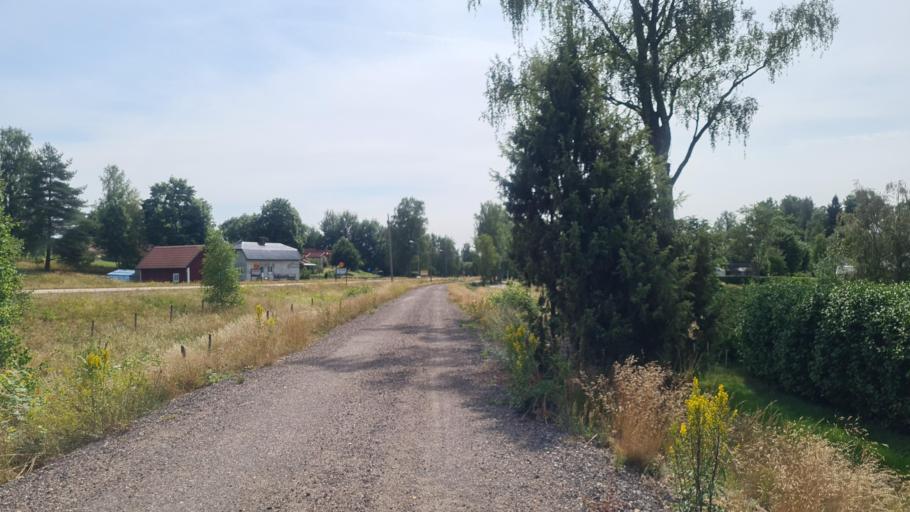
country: SE
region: Kronoberg
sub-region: Ljungby Kommun
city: Lagan
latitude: 56.9222
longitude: 13.9876
